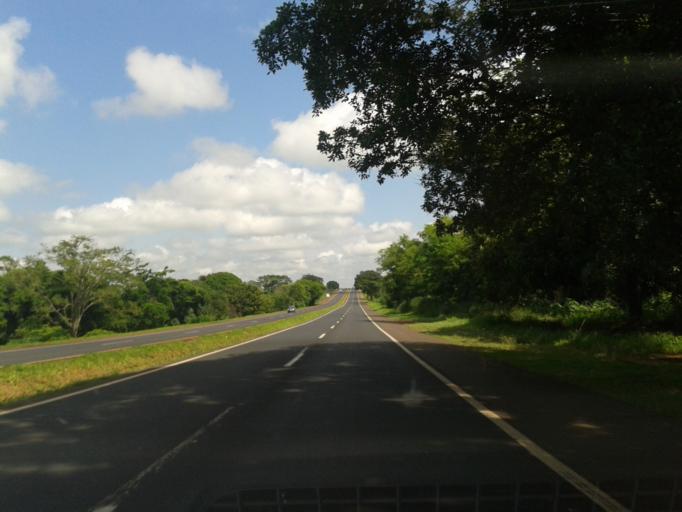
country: BR
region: Minas Gerais
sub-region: Centralina
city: Centralina
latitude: -18.6613
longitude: -49.1664
